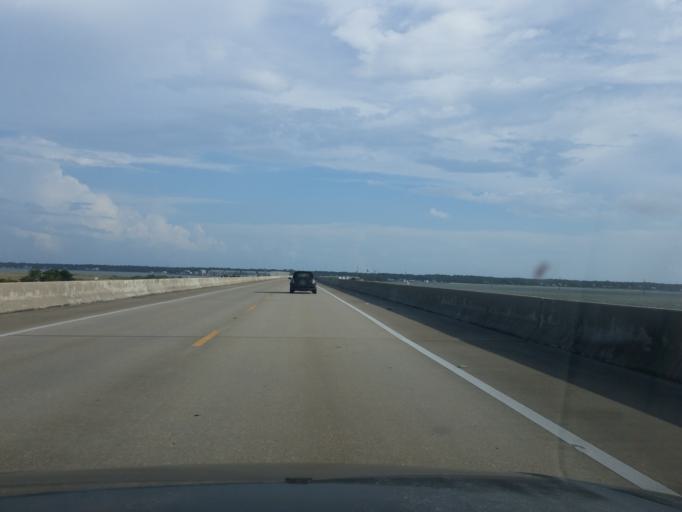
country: US
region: Alabama
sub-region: Mobile County
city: Dauphin Island
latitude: 30.2774
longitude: -88.1224
